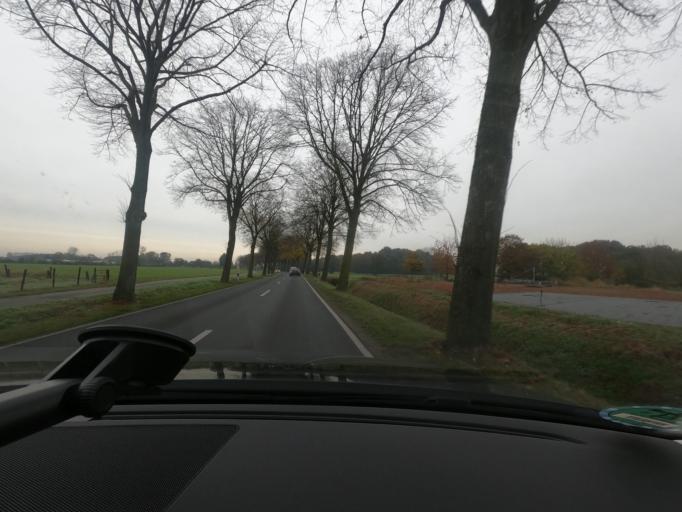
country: DE
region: North Rhine-Westphalia
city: Geldern
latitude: 51.5539
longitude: 6.2968
